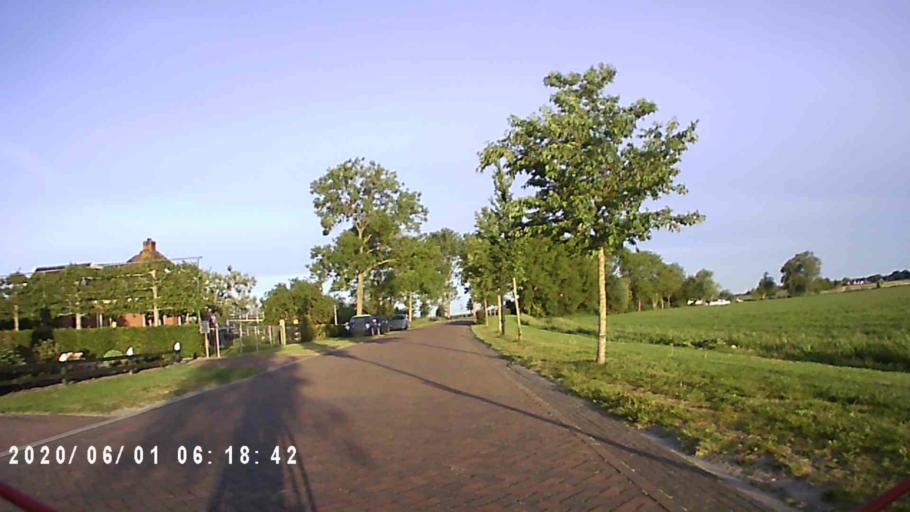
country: NL
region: Groningen
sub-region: Gemeente Grootegast
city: Grootegast
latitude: 53.2658
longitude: 6.2462
